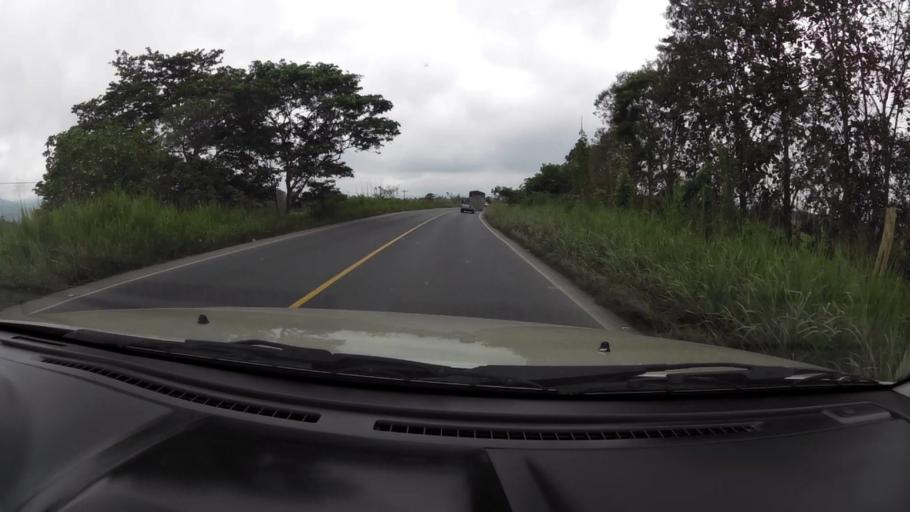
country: EC
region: Guayas
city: Balao
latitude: -2.8168
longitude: -79.7085
